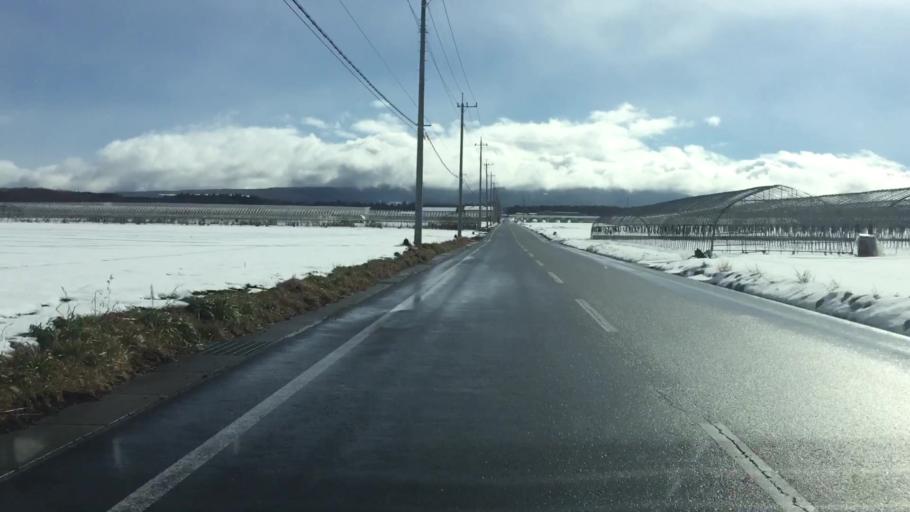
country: JP
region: Gunma
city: Numata
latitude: 36.6353
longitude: 139.0840
